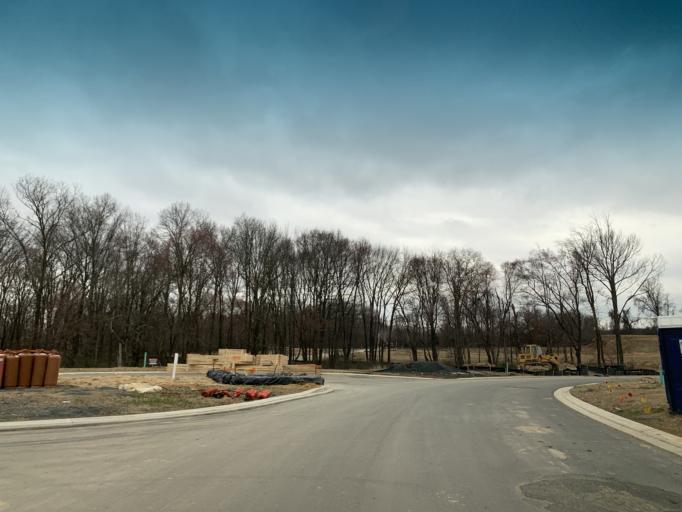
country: US
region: Maryland
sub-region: Harford County
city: Aberdeen
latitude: 39.5418
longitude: -76.1902
